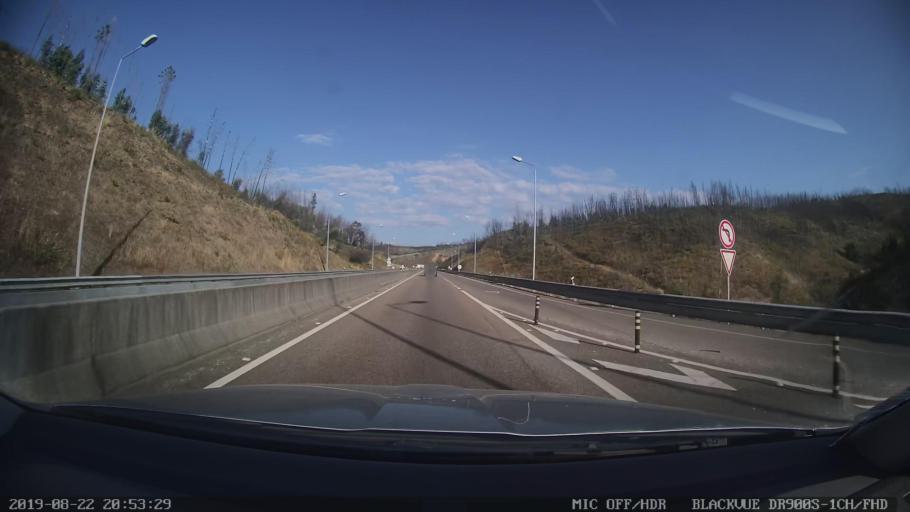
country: PT
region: Castelo Branco
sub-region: Proenca-A-Nova
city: Proenca-a-Nova
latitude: 39.7706
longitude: -7.9929
